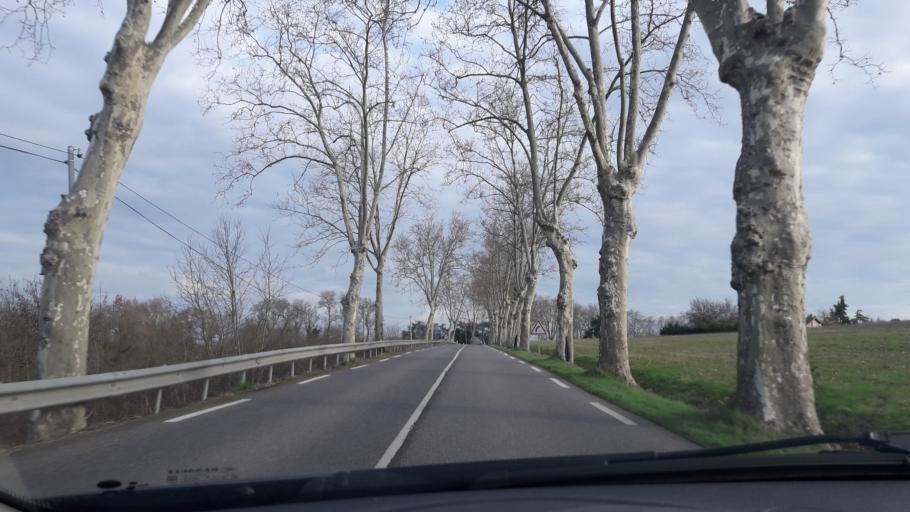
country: FR
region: Midi-Pyrenees
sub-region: Departement de la Haute-Garonne
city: Grenade
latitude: 43.7464
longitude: 1.2652
